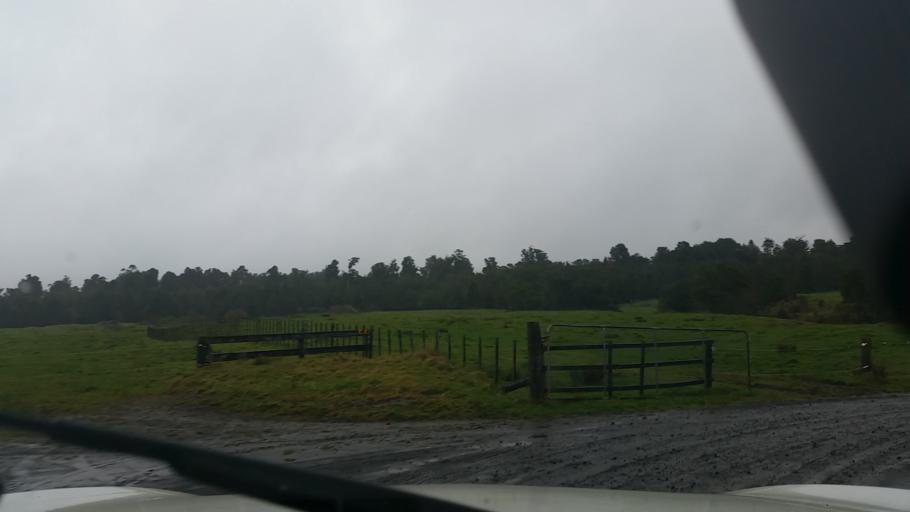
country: NZ
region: Taranaki
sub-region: South Taranaki District
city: Eltham
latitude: -39.2805
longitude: 174.1789
